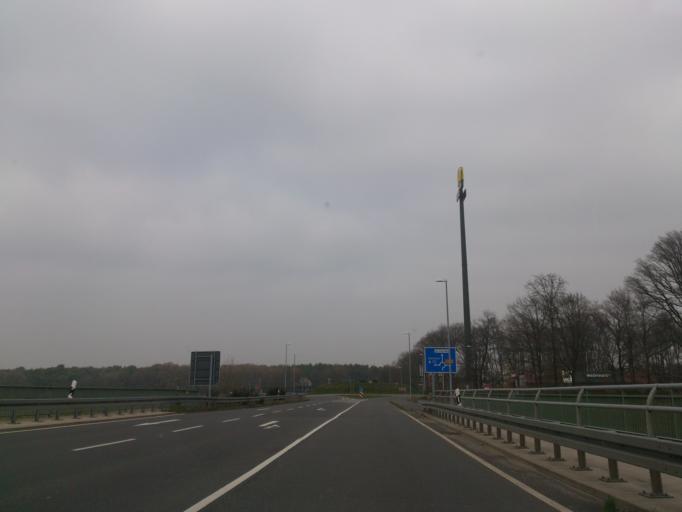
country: DE
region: North Rhine-Westphalia
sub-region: Regierungsbezirk Dusseldorf
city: Bruggen
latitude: 51.2106
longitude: 6.1335
